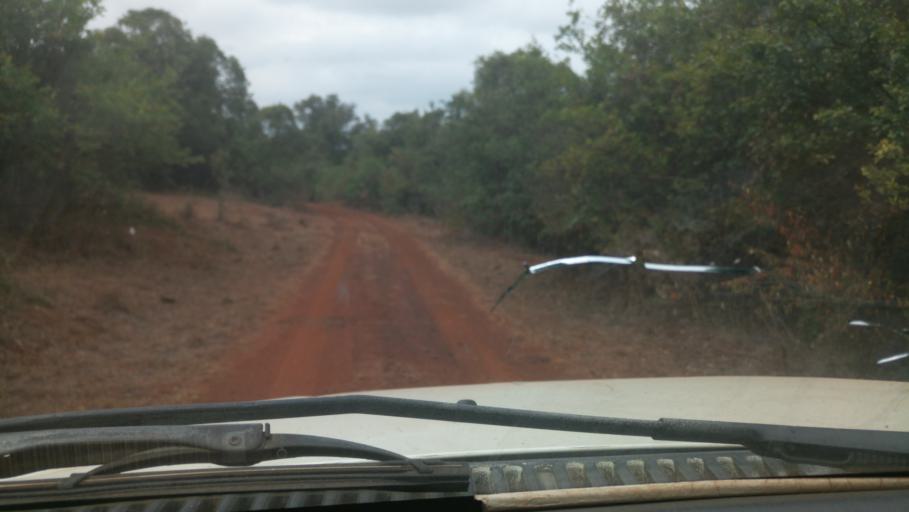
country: KE
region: Nairobi Area
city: Nairobi
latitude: -1.3499
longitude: 36.7757
